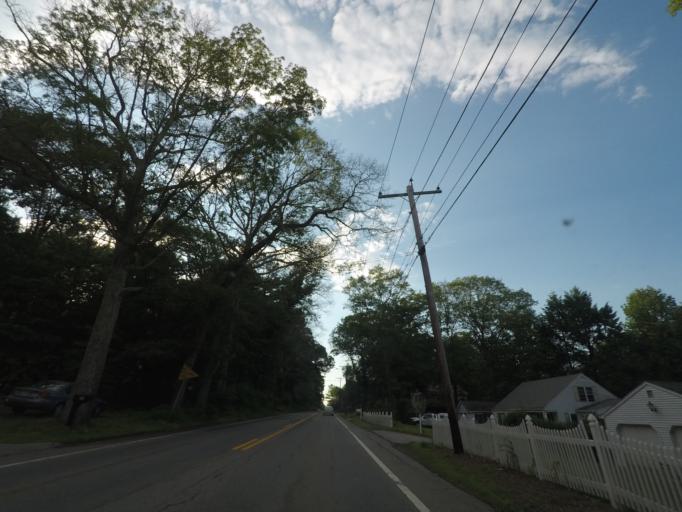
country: US
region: Connecticut
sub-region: Windham County
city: Quinebaug
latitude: 42.0350
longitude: -71.9679
